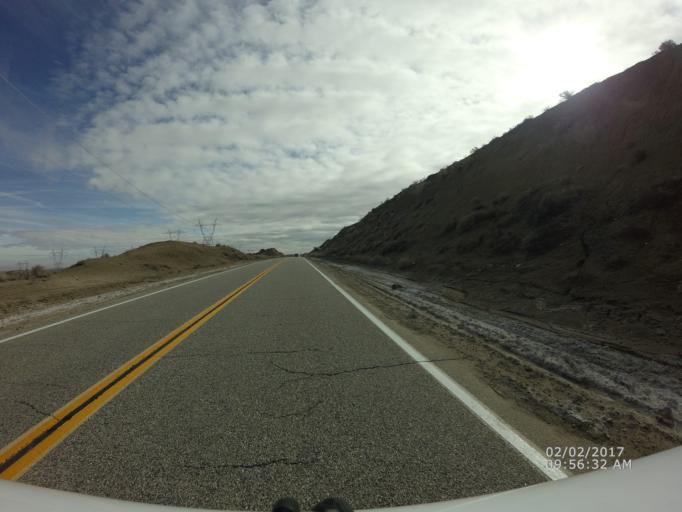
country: US
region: California
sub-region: Los Angeles County
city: Littlerock
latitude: 34.5065
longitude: -118.0156
